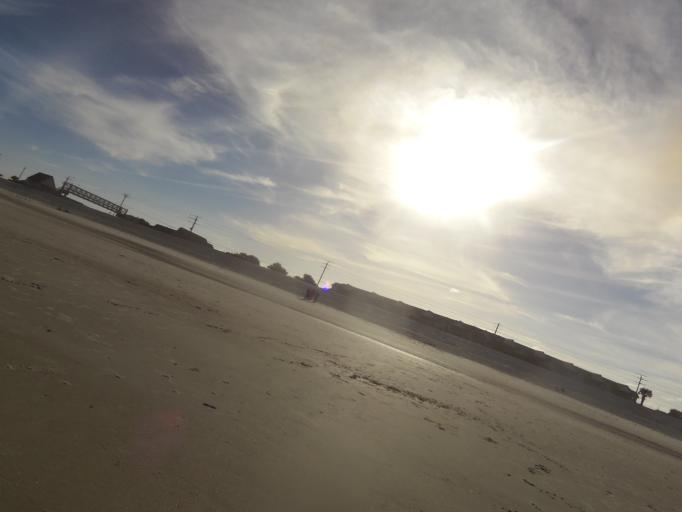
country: US
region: Florida
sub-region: Saint Johns County
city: Villano Beach
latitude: 29.9395
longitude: -81.2987
